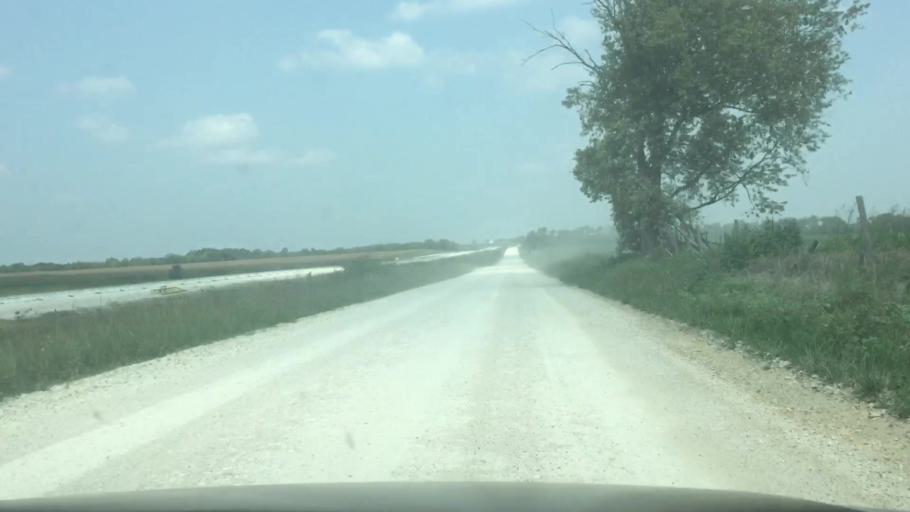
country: US
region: Kansas
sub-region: Allen County
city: Humboldt
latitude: 37.8333
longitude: -95.4094
